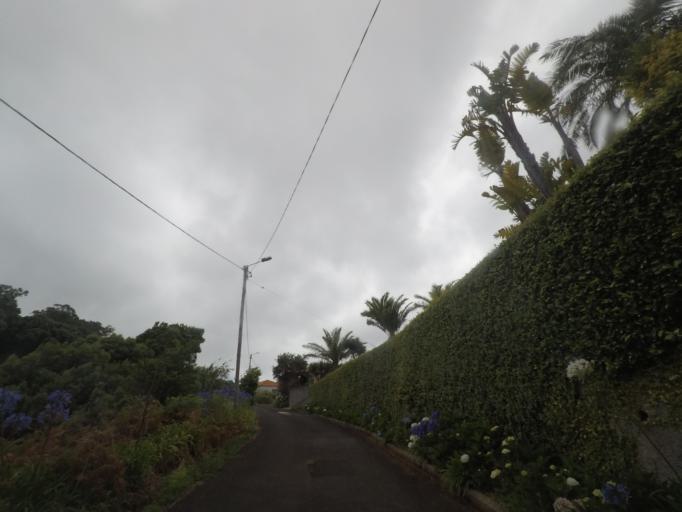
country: PT
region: Madeira
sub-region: Porto Moniz
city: Porto Moniz
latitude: 32.8617
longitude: -17.1847
